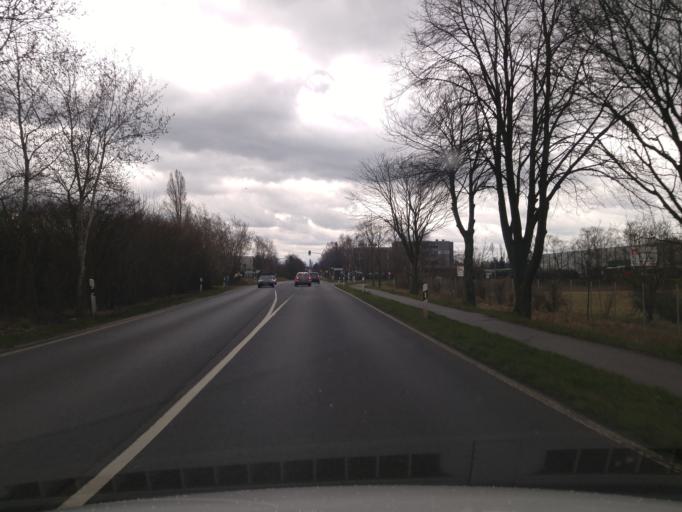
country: DE
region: North Rhine-Westphalia
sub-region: Regierungsbezirk Dusseldorf
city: Dormagen
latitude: 51.1420
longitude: 6.7969
